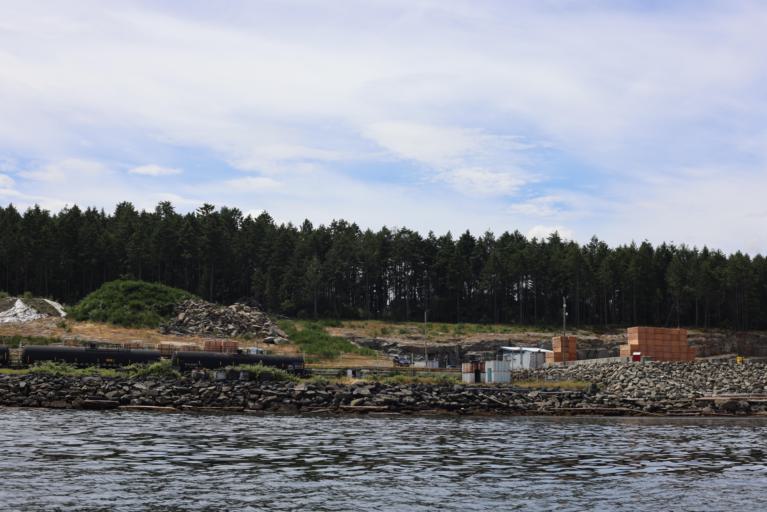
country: CA
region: British Columbia
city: Nanaimo
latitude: 49.1427
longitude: -123.8683
